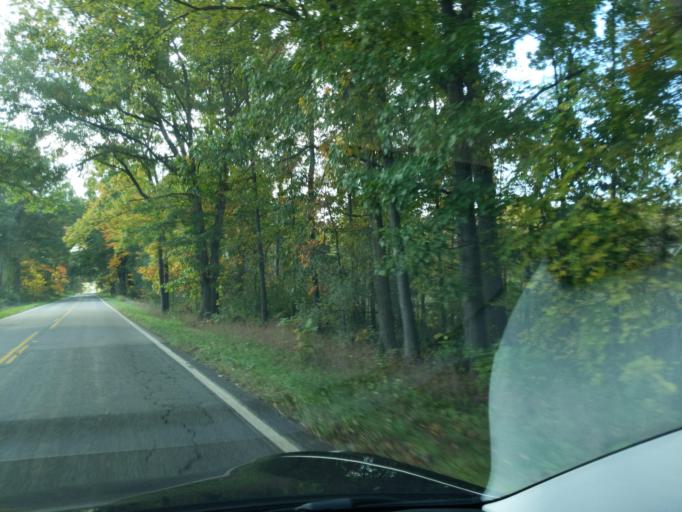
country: US
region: Michigan
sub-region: Ingham County
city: Leslie
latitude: 42.3713
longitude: -84.4515
